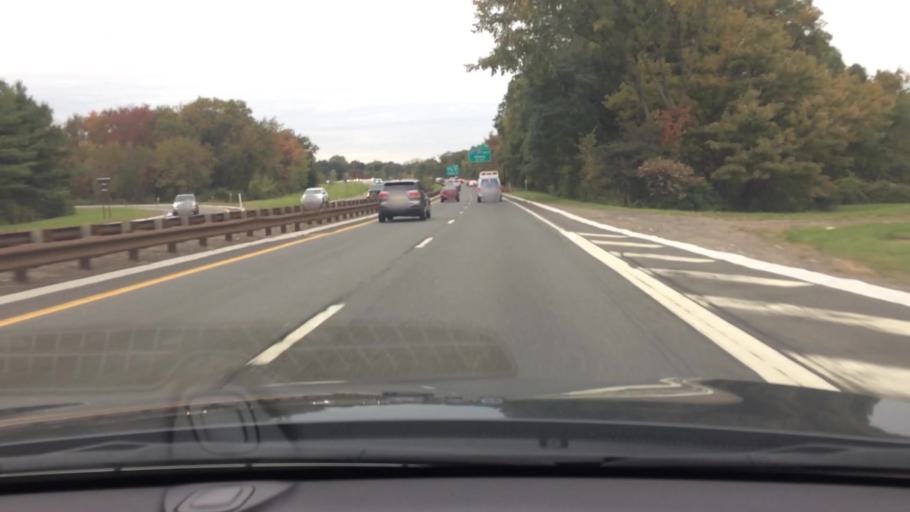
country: US
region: New York
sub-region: Rockland County
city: Bardonia
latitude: 41.0978
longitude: -73.9913
